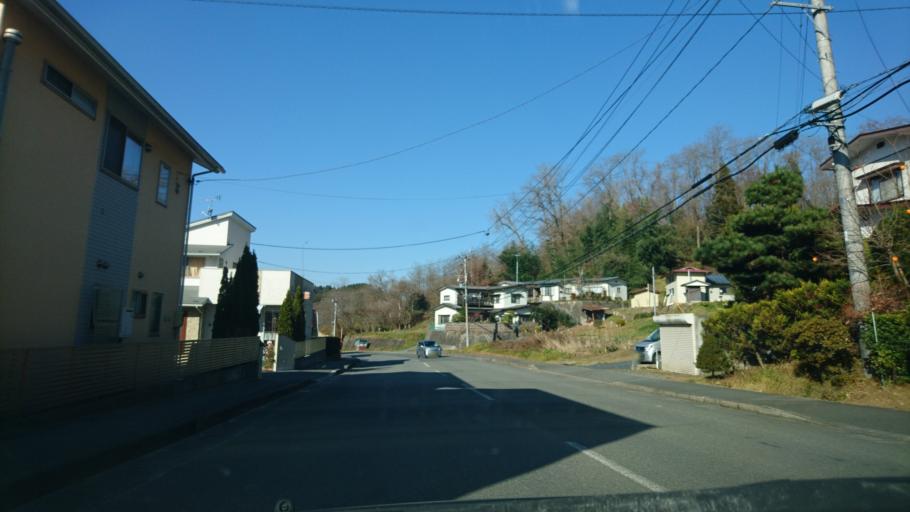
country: JP
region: Iwate
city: Ichinoseki
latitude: 38.9168
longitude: 141.3415
